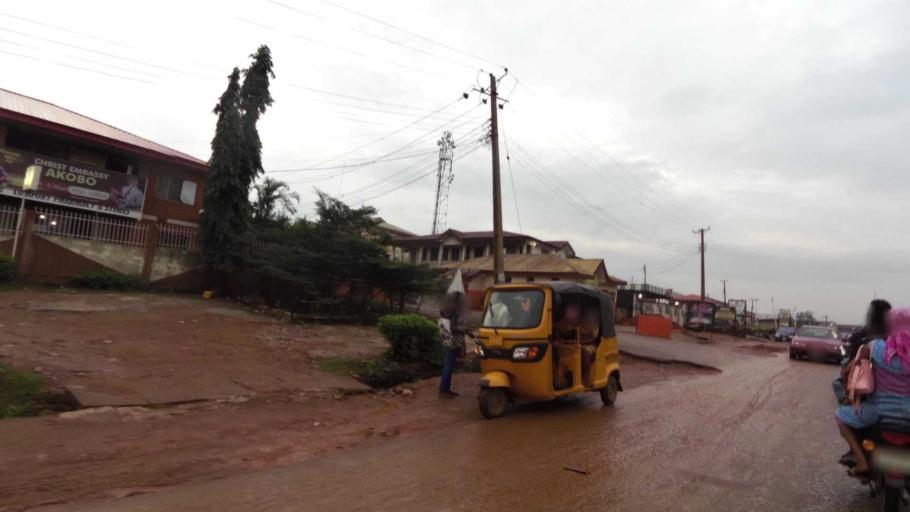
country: NG
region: Oyo
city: Ibadan
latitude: 7.4306
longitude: 3.9405
